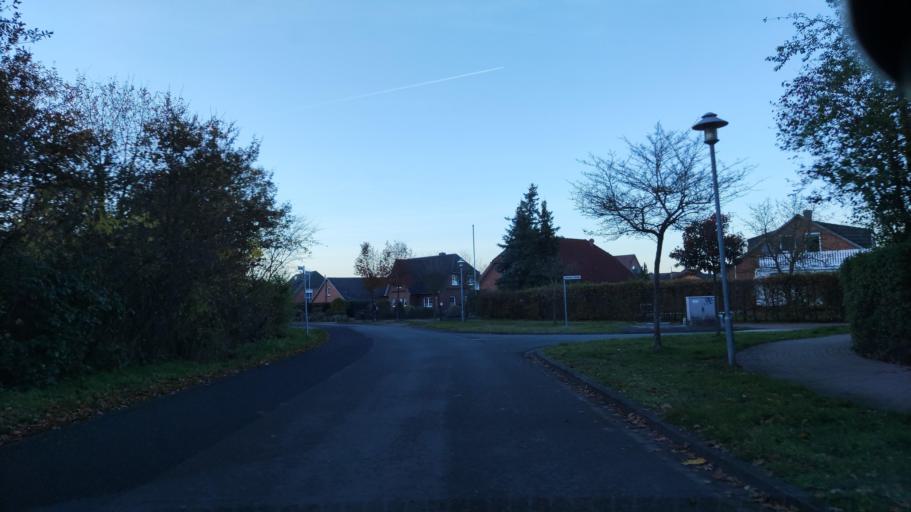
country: DE
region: Lower Saxony
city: Bleckede
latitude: 53.2802
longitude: 10.7350
